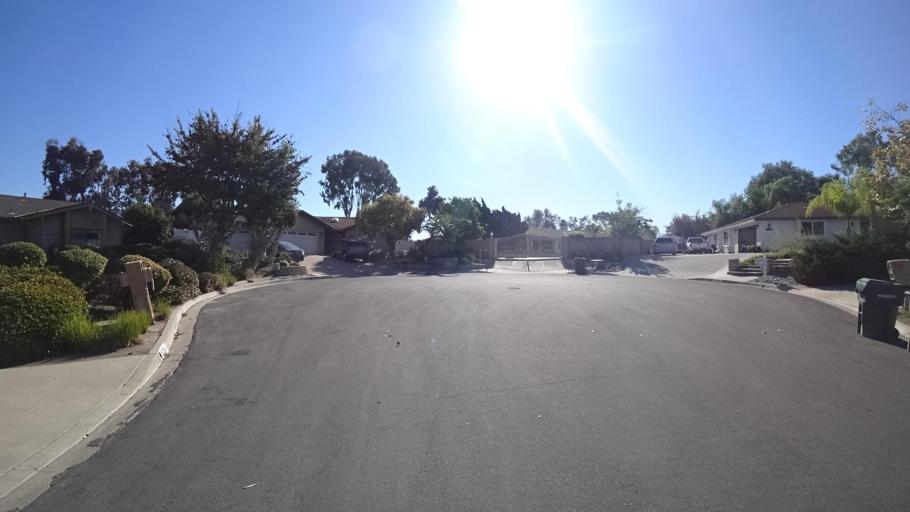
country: US
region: California
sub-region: San Diego County
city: Bonita
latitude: 32.6743
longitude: -117.0053
